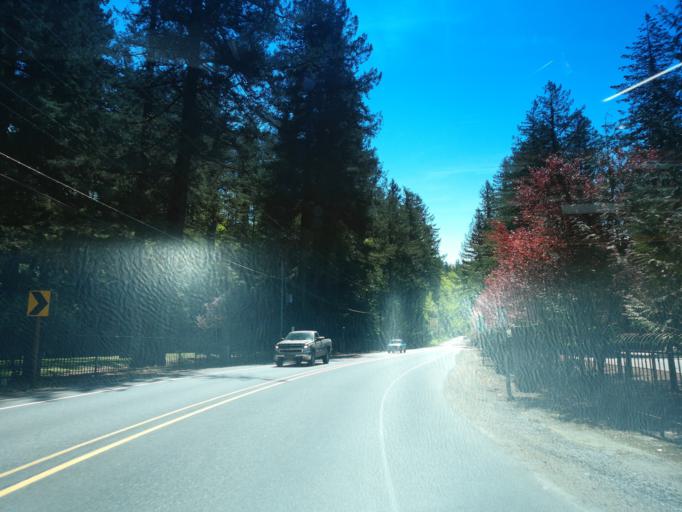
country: US
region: Oregon
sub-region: Multnomah County
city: Troutdale
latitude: 45.5144
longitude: -122.3609
